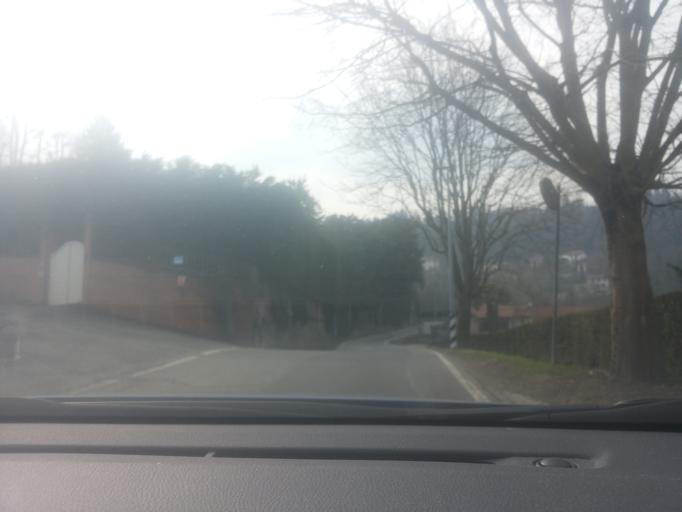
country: IT
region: Piedmont
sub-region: Provincia di Torino
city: Turin
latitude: 45.0564
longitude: 7.7214
